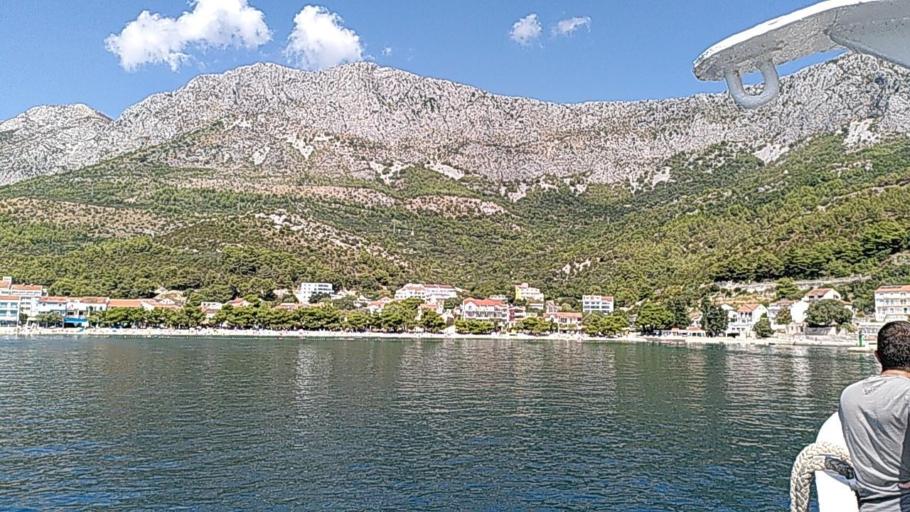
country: HR
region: Splitsko-Dalmatinska
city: Vrgorac
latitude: 43.1528
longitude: 17.2469
